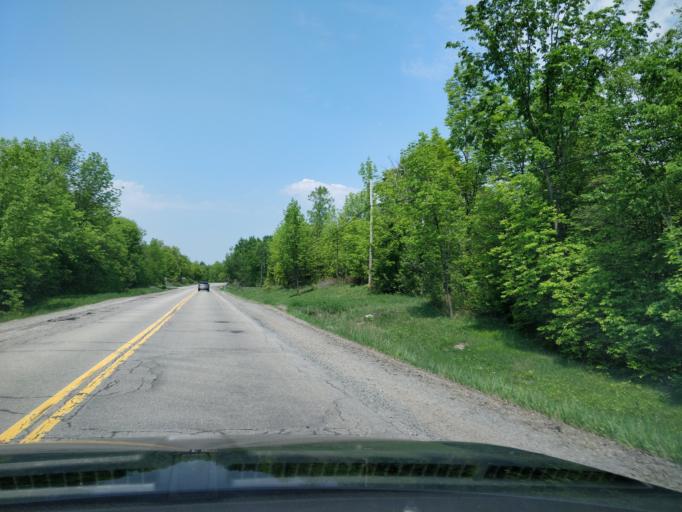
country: CA
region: Ontario
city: Perth
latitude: 44.7147
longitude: -76.4014
